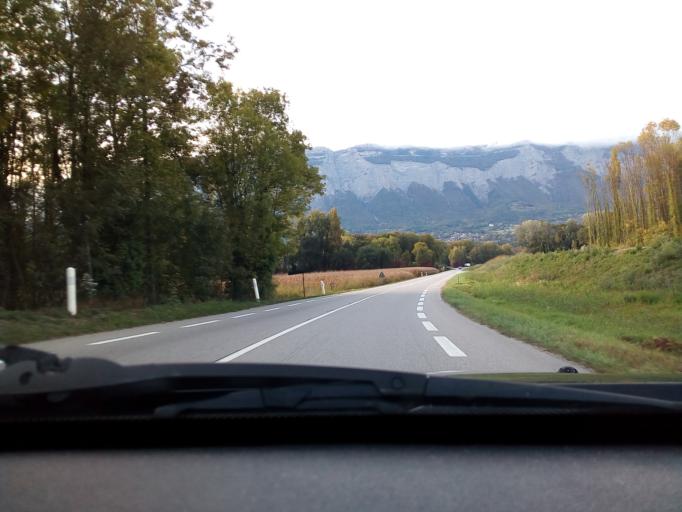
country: FR
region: Rhone-Alpes
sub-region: Departement de l'Isere
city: Domene
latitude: 45.2136
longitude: 5.8267
